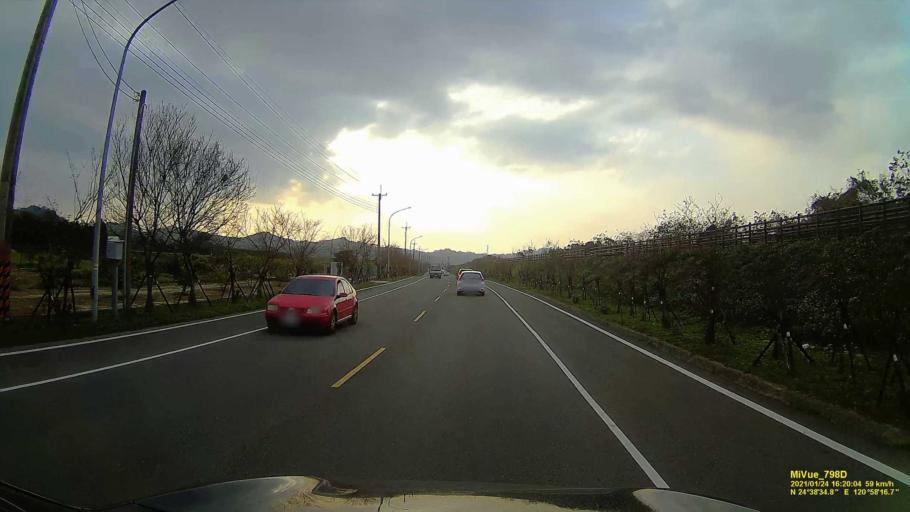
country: TW
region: Taiwan
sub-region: Hsinchu
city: Hsinchu
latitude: 24.6430
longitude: 120.9710
